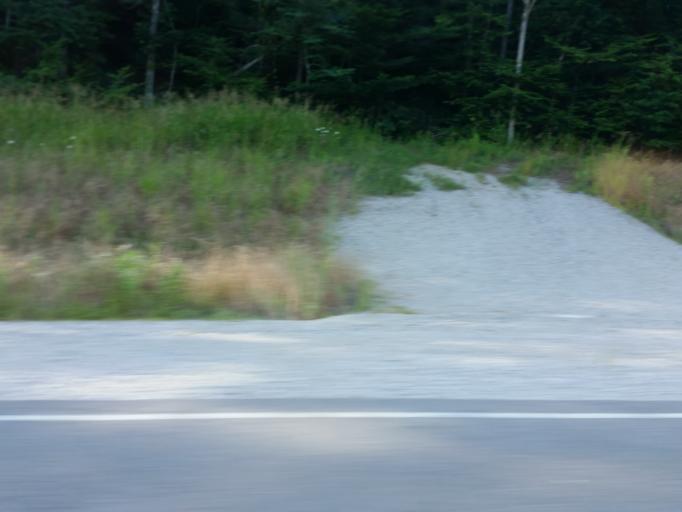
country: US
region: Tennessee
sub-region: Maury County
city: Mount Pleasant
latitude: 35.5641
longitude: -87.3768
